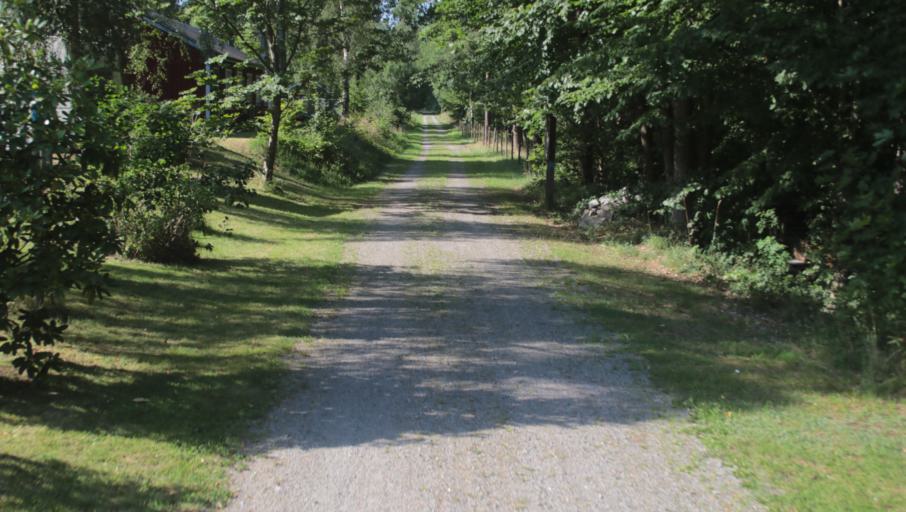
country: SE
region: Blekinge
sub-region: Karlshamns Kommun
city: Svangsta
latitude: 56.2915
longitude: 14.7435
